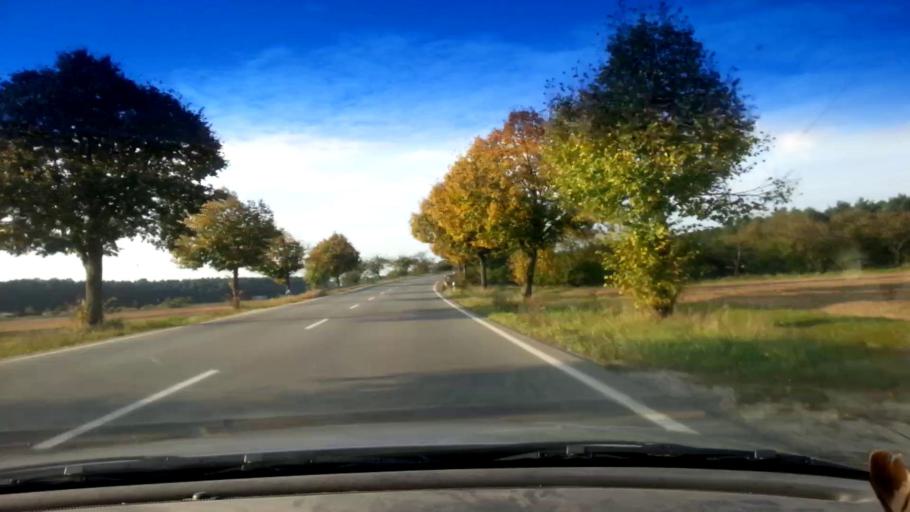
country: DE
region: Bavaria
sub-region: Upper Franconia
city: Hirschaid
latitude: 49.8245
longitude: 10.9836
